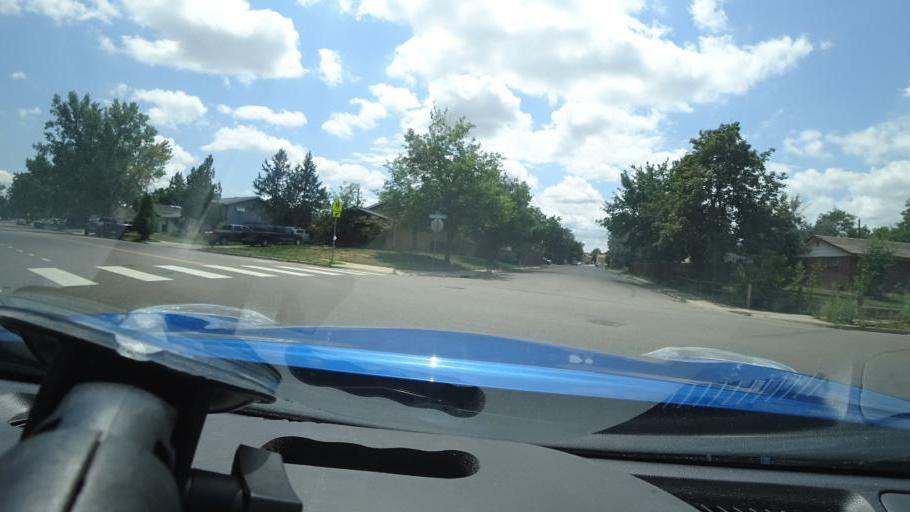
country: US
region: Colorado
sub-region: Adams County
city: Aurora
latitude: 39.7032
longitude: -104.8429
